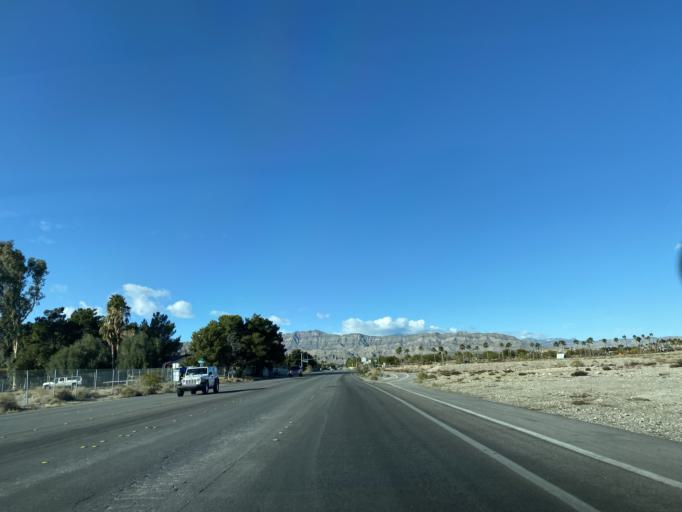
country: US
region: Nevada
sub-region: Clark County
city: Summerlin South
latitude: 36.2702
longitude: -115.2757
